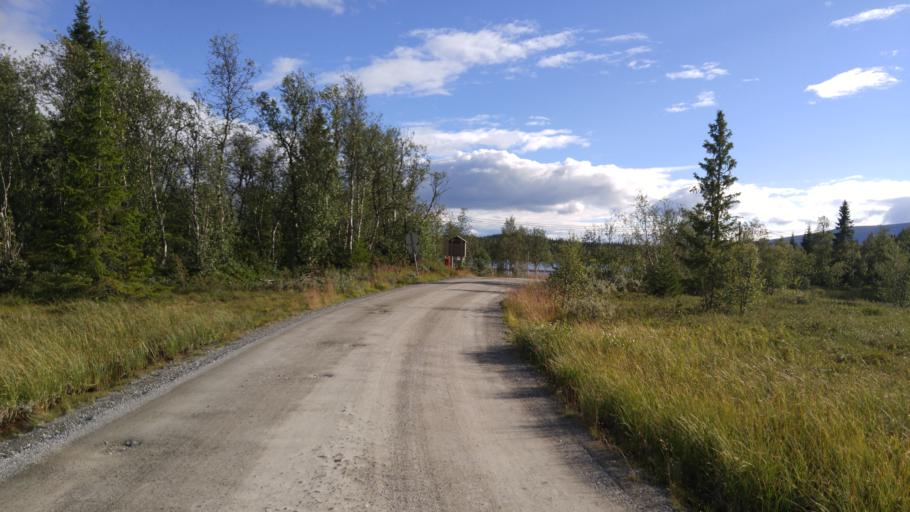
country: NO
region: Buskerud
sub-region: Hemsedal
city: Troim
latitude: 60.8465
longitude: 8.7237
